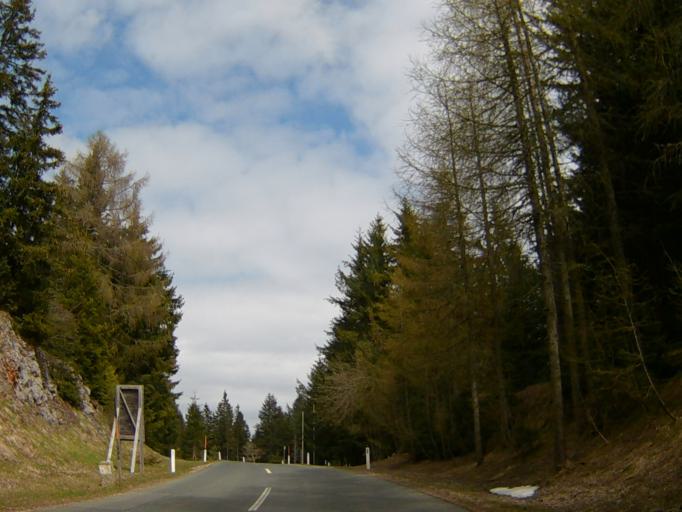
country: AT
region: Carinthia
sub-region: Politischer Bezirk Villach Land
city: Arnoldstein
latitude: 46.5923
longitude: 13.7386
